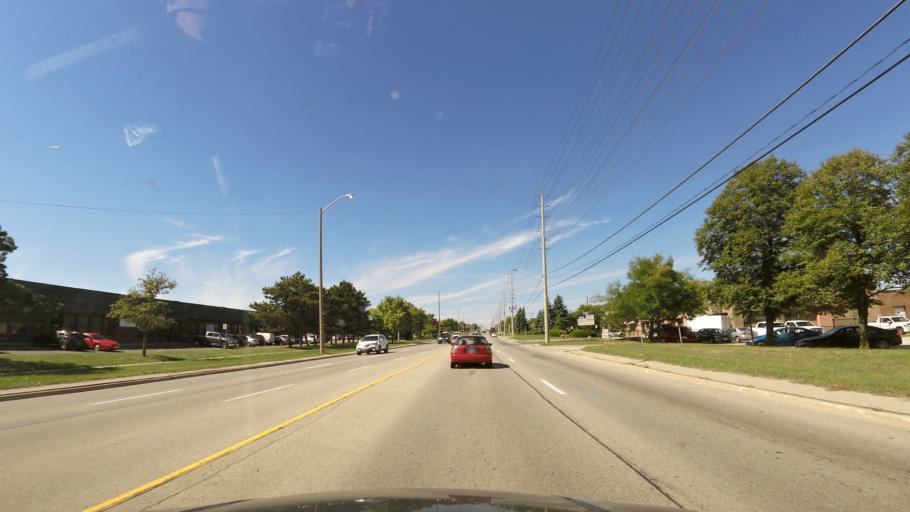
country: CA
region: Ontario
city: Mississauga
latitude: 43.6310
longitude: -79.6382
